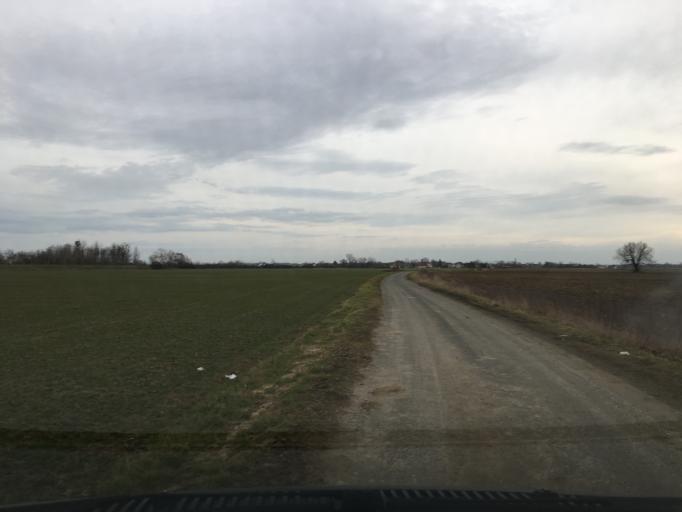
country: PL
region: Opole Voivodeship
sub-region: Powiat kedzierzynsko-kozielski
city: Wiekszyce
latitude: 50.3662
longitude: 18.1119
